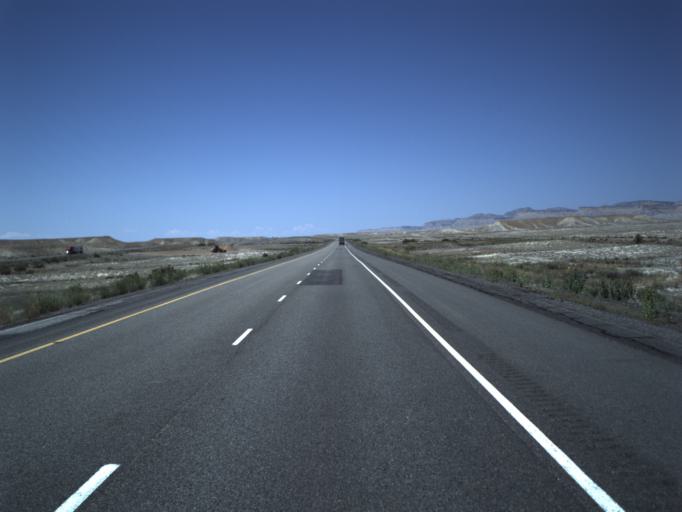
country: US
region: Utah
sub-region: Grand County
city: Moab
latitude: 38.9401
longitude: -109.5033
